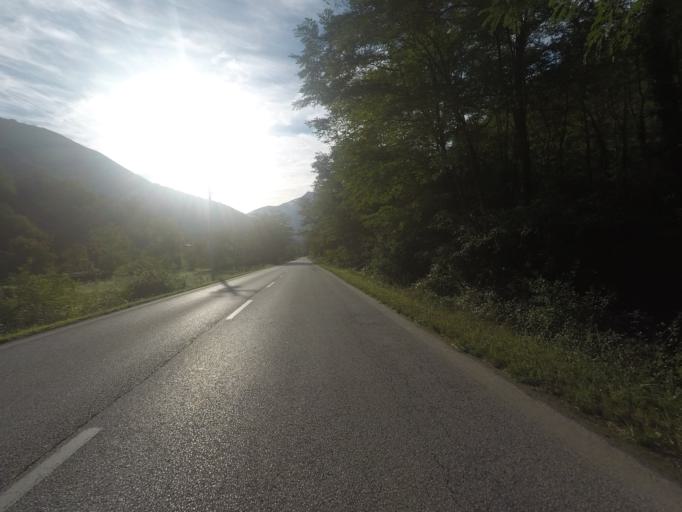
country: IT
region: Tuscany
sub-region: Provincia di Lucca
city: Valdottavo
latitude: 43.9697
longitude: 10.4896
